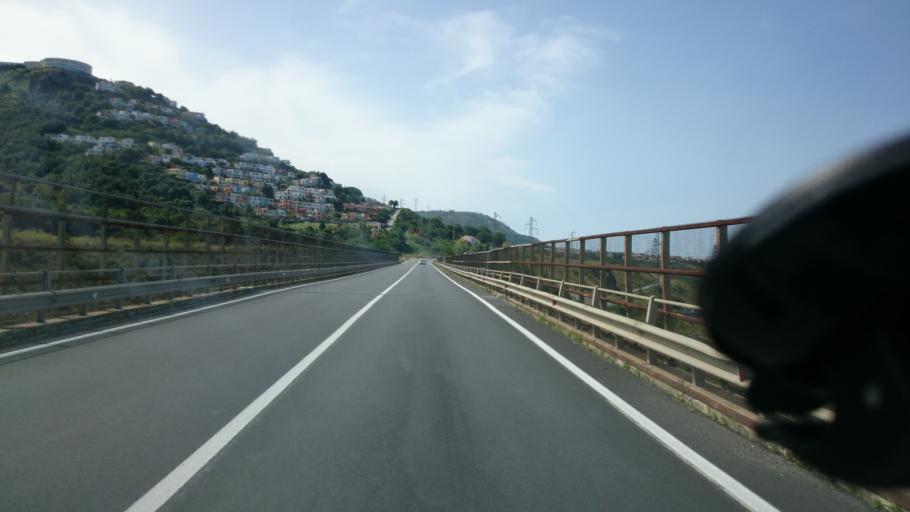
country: IT
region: Calabria
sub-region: Provincia di Cosenza
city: Praia a Mare
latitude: 39.8712
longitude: 15.7952
